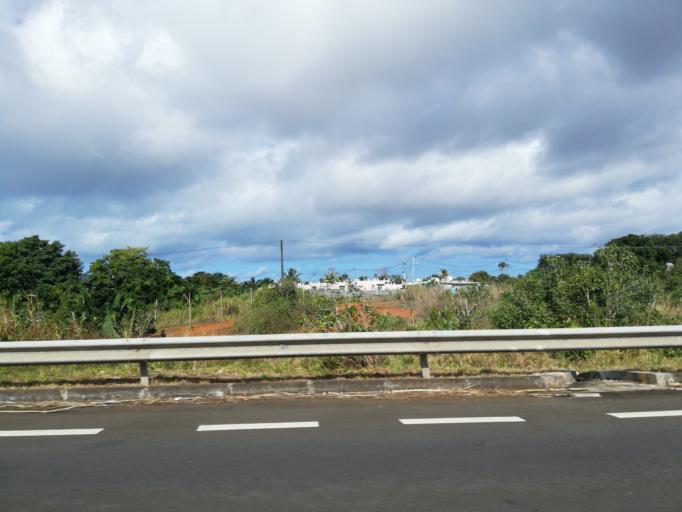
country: MU
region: Grand Port
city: Beau Vallon
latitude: -20.4061
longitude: 57.6755
